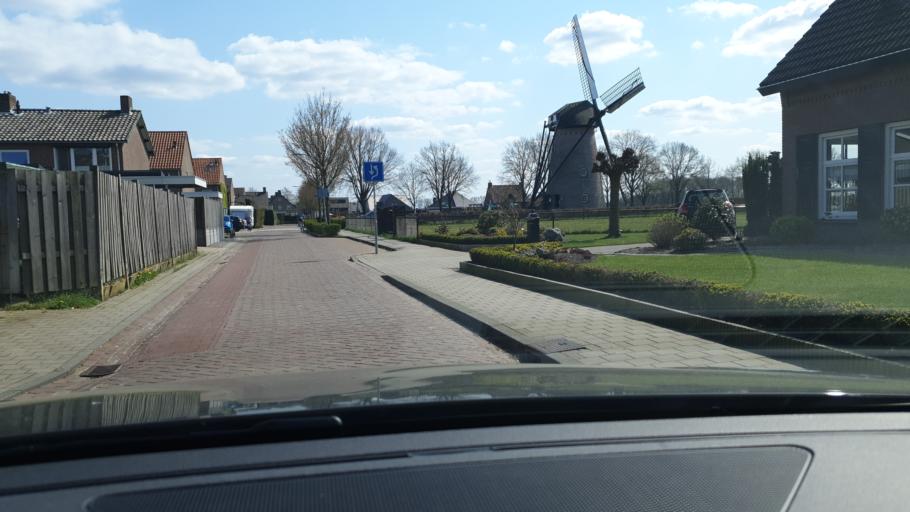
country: NL
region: North Brabant
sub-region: Gemeente Bladel en Netersel
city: Bladel
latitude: 51.3656
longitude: 5.2520
